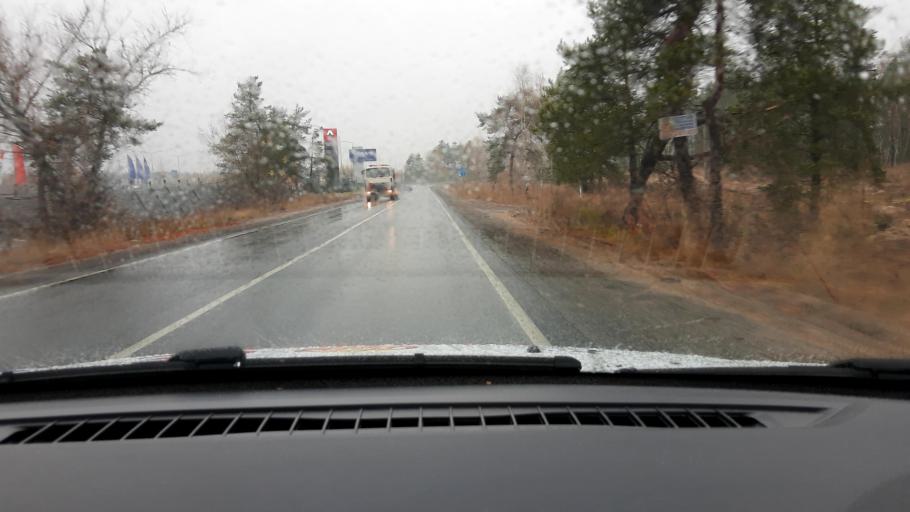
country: RU
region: Nizjnij Novgorod
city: Babino
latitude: 56.2991
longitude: 43.5955
